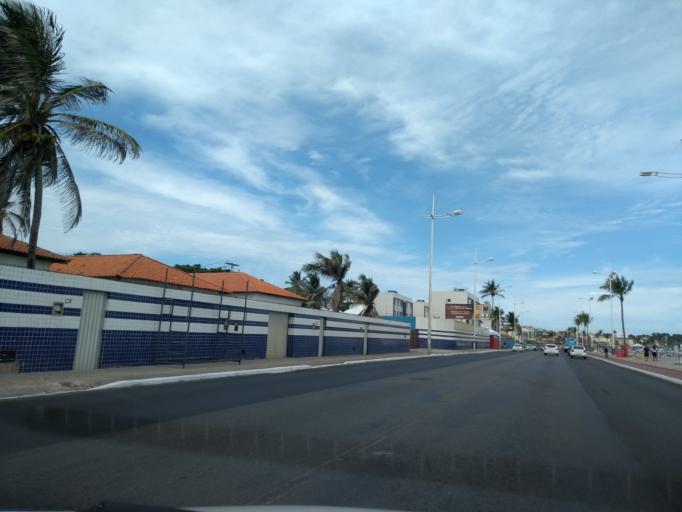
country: BR
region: Bahia
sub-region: Lauro De Freitas
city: Lauro de Freitas
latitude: -12.9514
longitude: -38.3727
